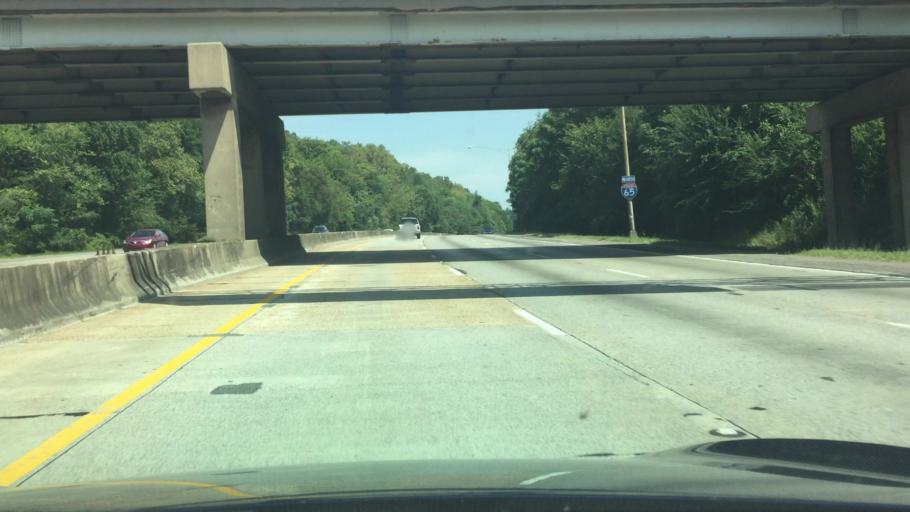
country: US
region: Alabama
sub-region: Jefferson County
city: Homewood
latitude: 33.4695
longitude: -86.8279
